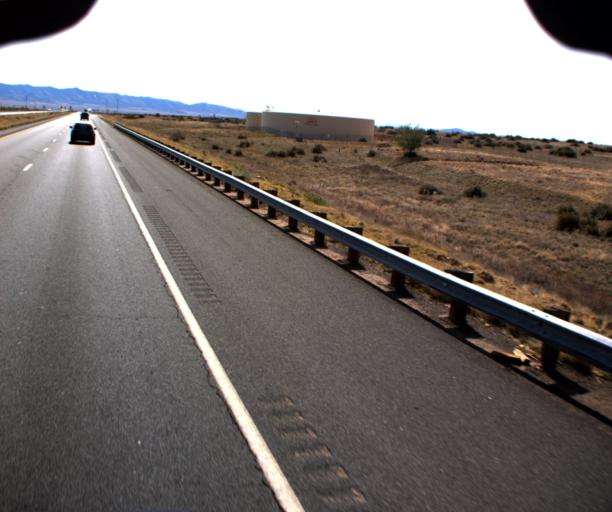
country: US
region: Arizona
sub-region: Yavapai County
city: Prescott Valley
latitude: 34.6306
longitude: -112.3797
